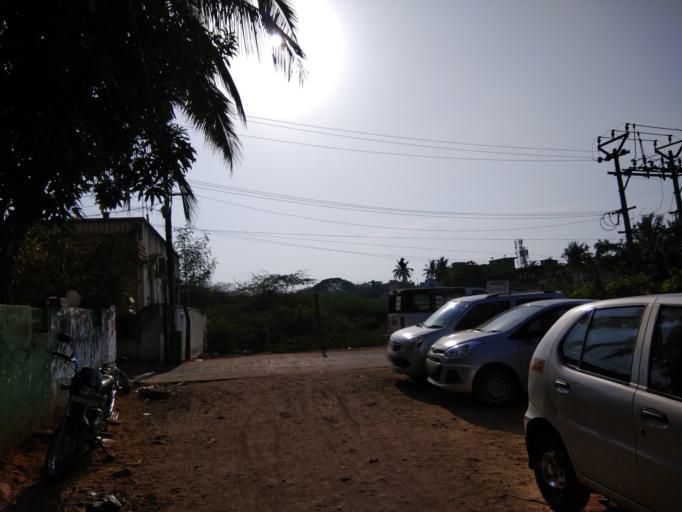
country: IN
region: Tamil Nadu
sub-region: Kancheepuram
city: Saint Thomas Mount
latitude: 13.0111
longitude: 80.1865
